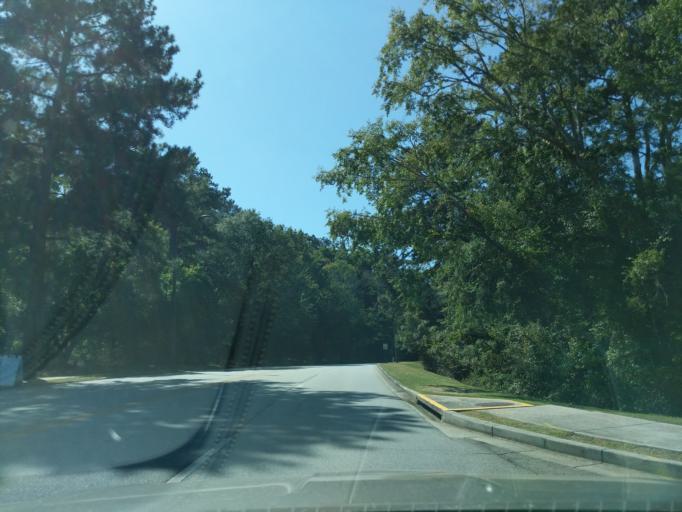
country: US
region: Georgia
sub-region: DeKalb County
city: Stone Mountain
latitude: 33.8123
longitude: -84.1513
